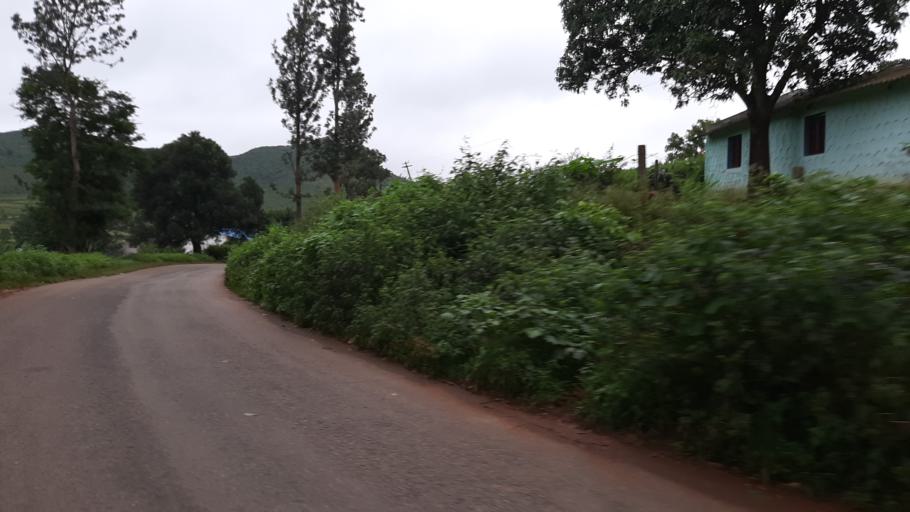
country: IN
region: Andhra Pradesh
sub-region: Vizianagaram District
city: Salur
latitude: 18.2854
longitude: 82.9390
